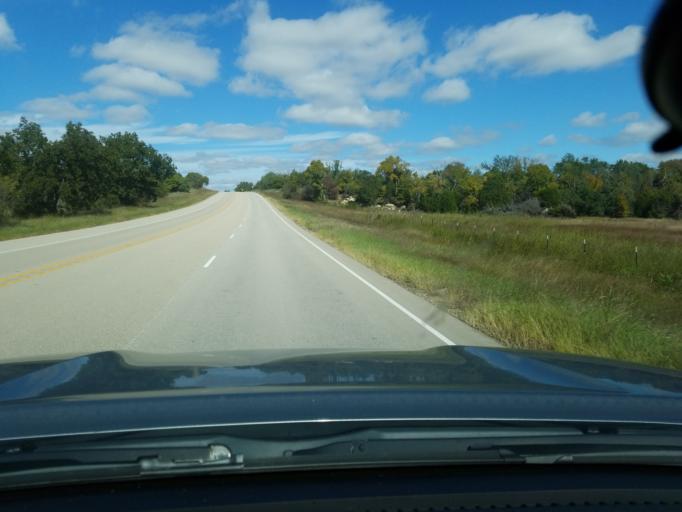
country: US
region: Texas
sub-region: Hamilton County
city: Hamilton
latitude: 31.5855
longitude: -98.1568
